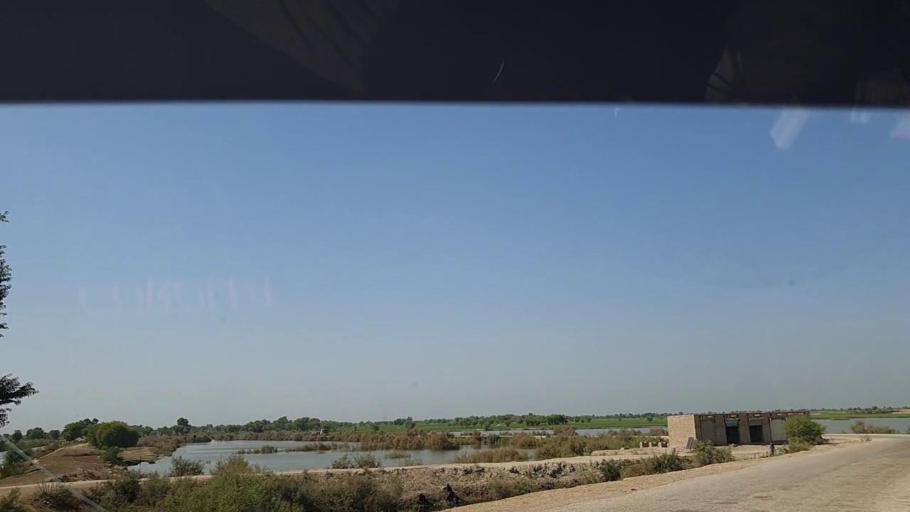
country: PK
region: Sindh
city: Ghauspur
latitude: 28.2013
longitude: 69.0410
